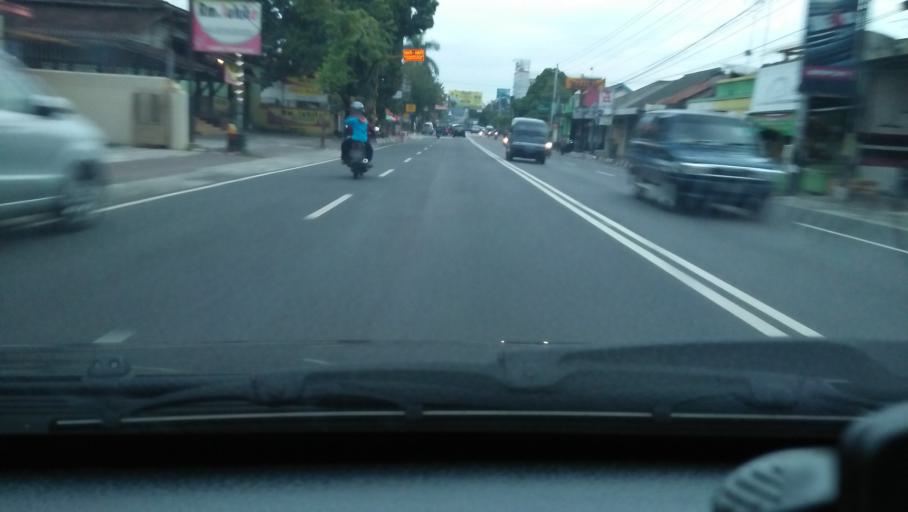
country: ID
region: Central Java
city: Magelang
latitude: -7.4506
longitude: 110.2242
